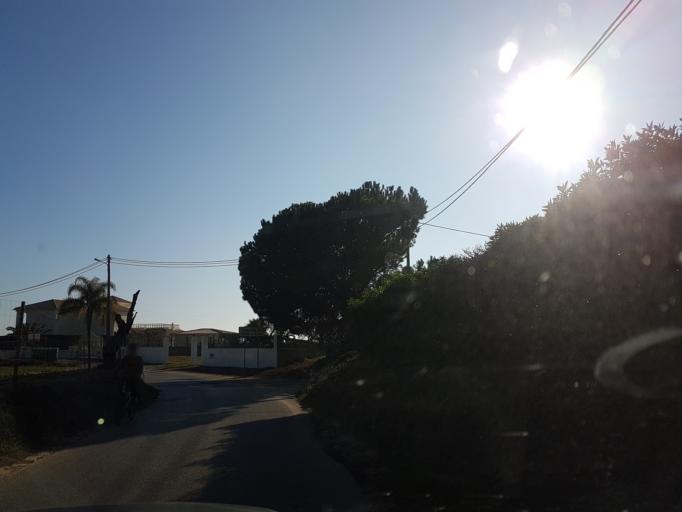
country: PT
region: Faro
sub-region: Albufeira
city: Ferreiras
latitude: 37.1032
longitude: -8.2078
